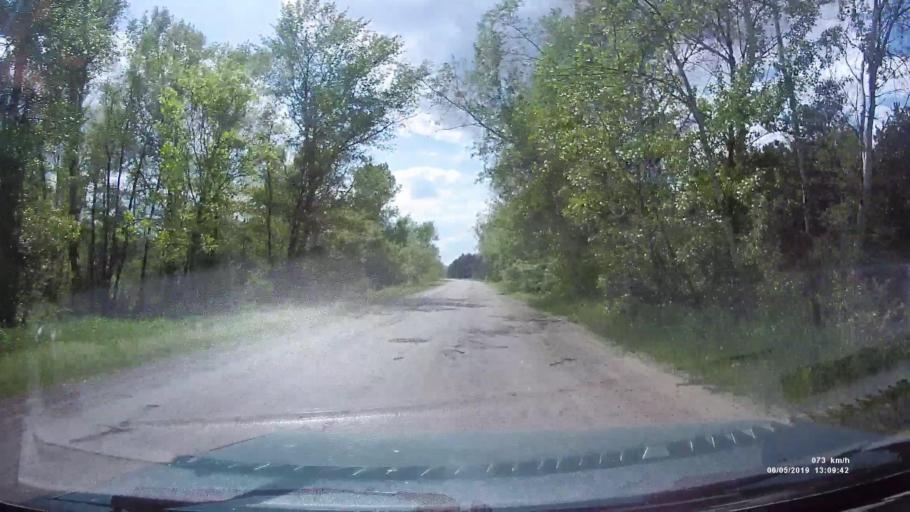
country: RU
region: Rostov
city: Ust'-Donetskiy
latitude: 47.7664
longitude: 40.9806
